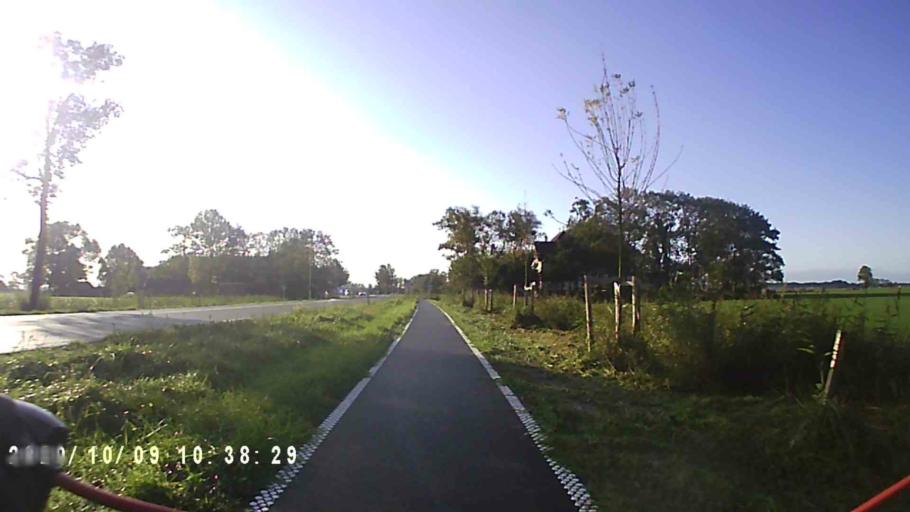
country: NL
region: Groningen
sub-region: Gemeente Winsum
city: Winsum
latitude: 53.2883
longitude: 6.5331
